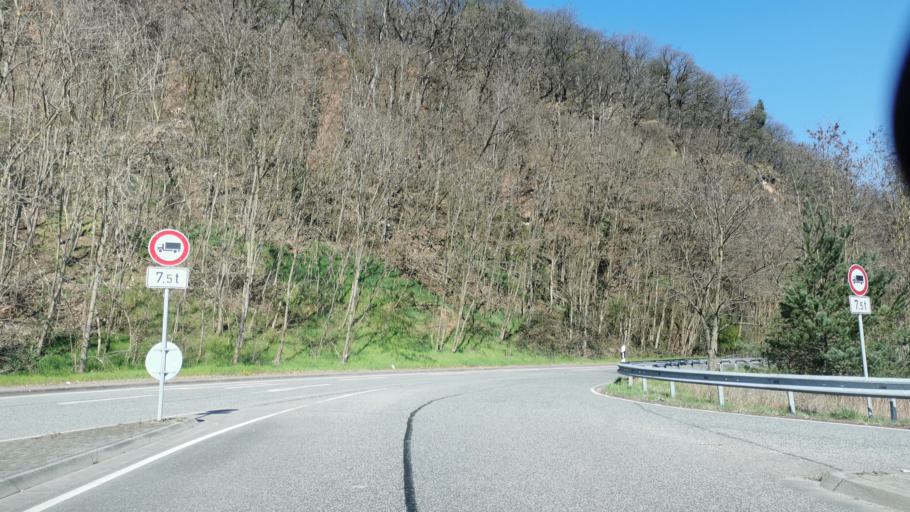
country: DE
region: Rheinland-Pfalz
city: Trier
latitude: 49.7745
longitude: 6.6555
